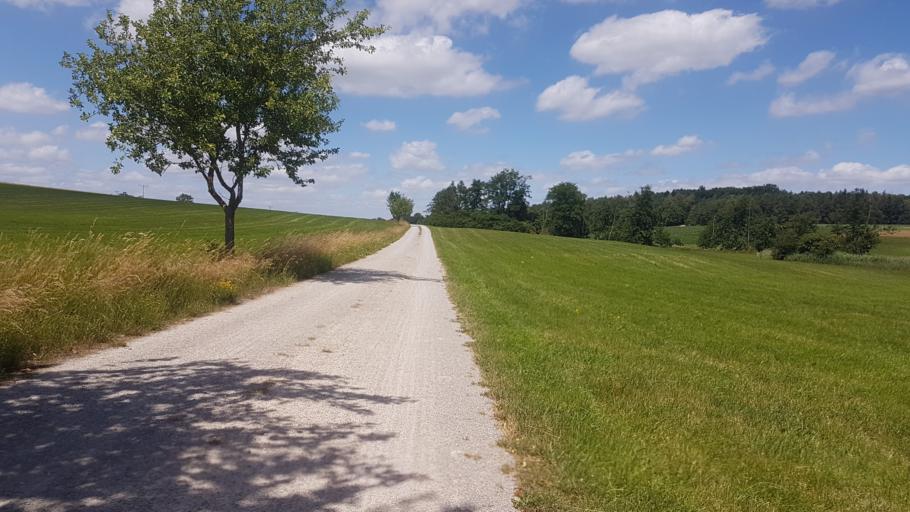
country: DE
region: Bavaria
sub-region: Regierungsbezirk Mittelfranken
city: Leutershausen
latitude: 49.3176
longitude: 10.3865
